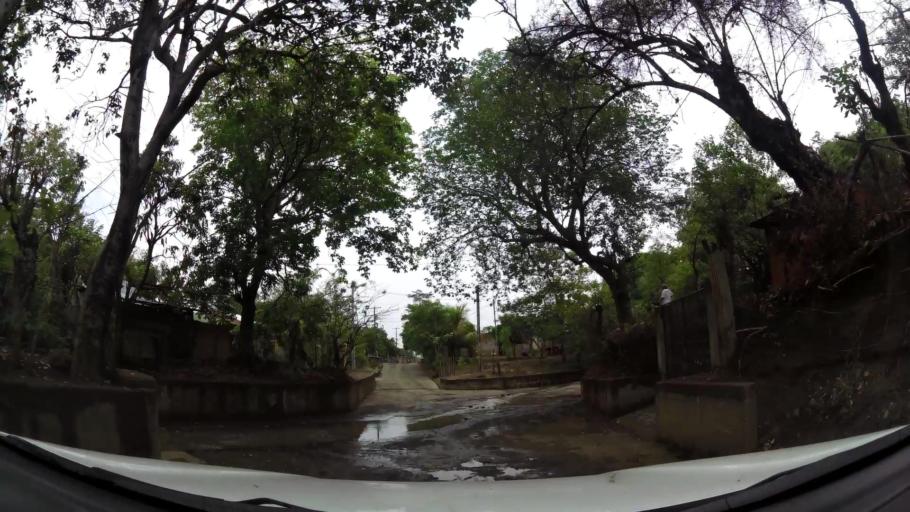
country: NI
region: Granada
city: Nandaime
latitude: 11.7546
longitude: -86.0476
